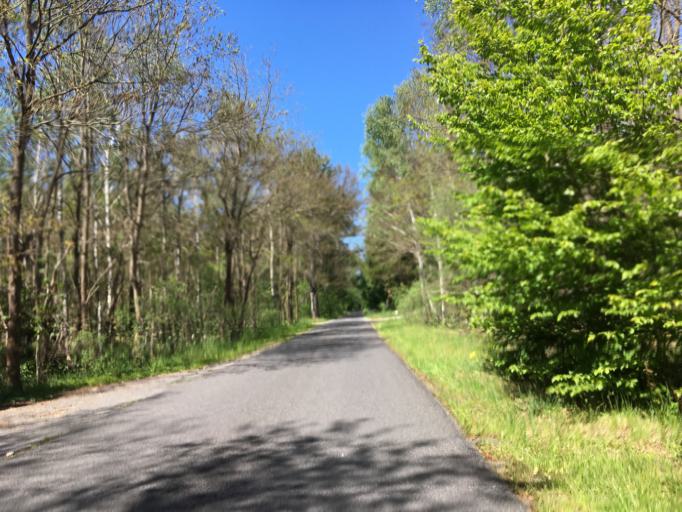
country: DE
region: Brandenburg
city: Zehdenick
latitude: 52.9920
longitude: 13.4283
